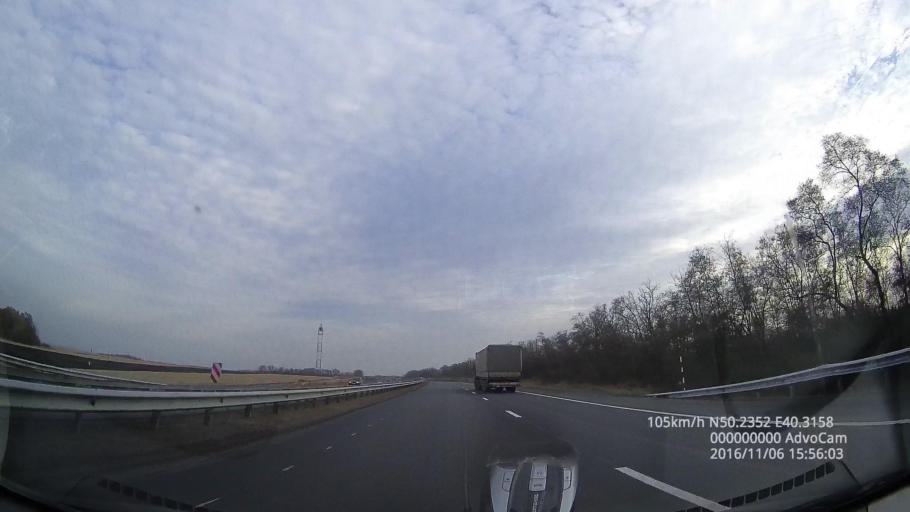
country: RU
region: Voronezj
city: Verkhniy Mamon
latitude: 50.2348
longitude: 40.3159
